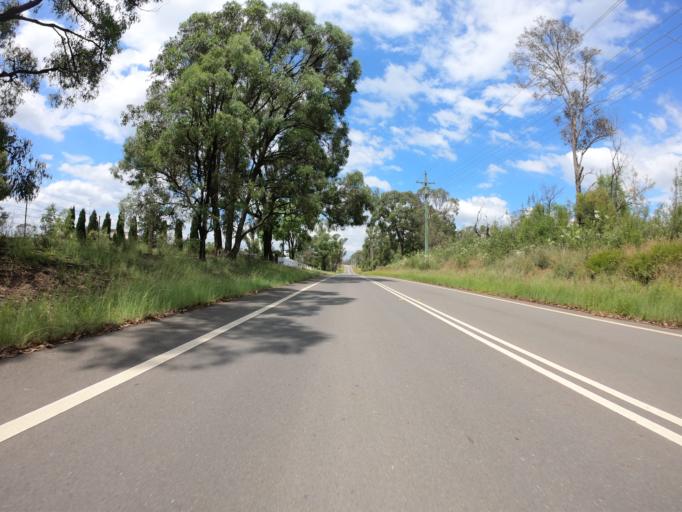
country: AU
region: New South Wales
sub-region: Penrith Municipality
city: Mulgoa
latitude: -33.8288
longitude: 150.6748
